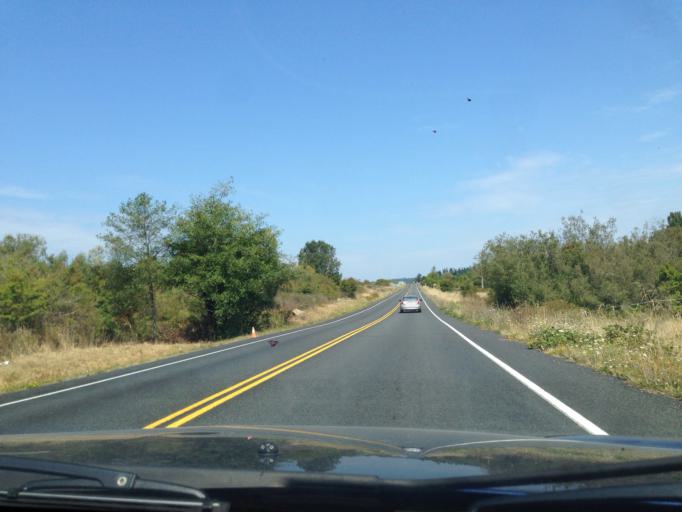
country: US
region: Washington
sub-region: San Juan County
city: Friday Harbor
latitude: 48.5133
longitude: -123.0230
